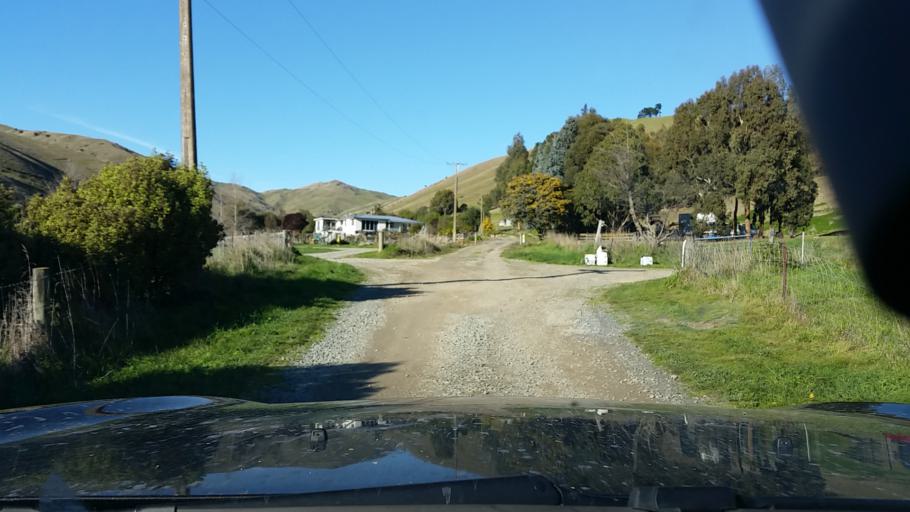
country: NZ
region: Marlborough
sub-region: Marlborough District
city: Blenheim
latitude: -41.5440
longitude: 173.9628
